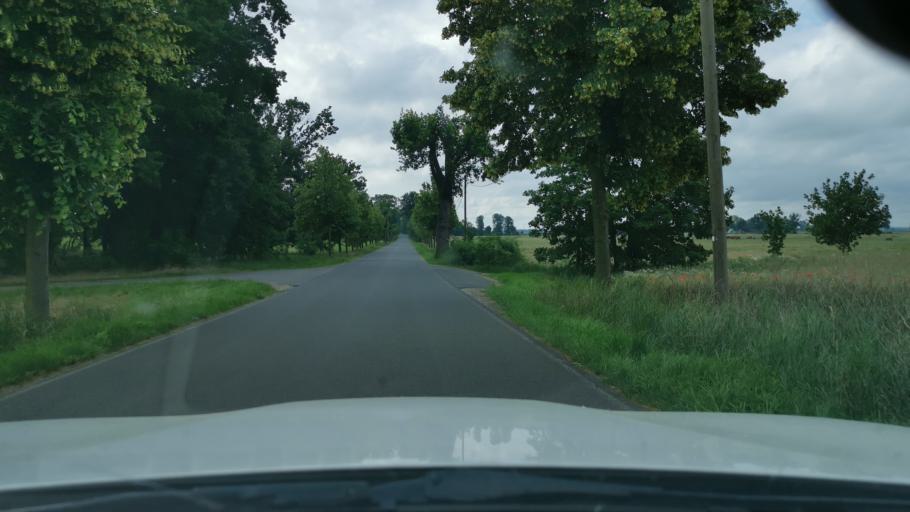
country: DE
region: Saxony
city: Torgau
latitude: 51.6111
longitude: 13.0180
